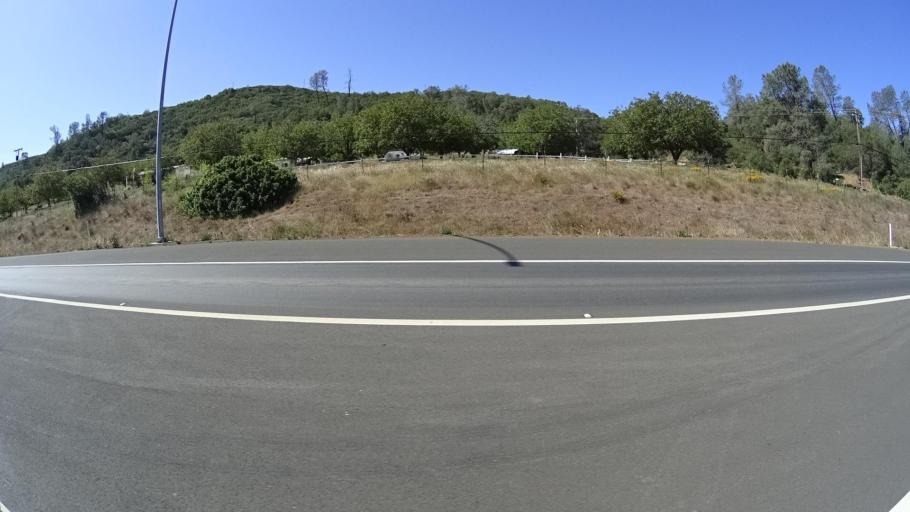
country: US
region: California
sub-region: Lake County
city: Clearlake
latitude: 39.0088
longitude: -122.6169
